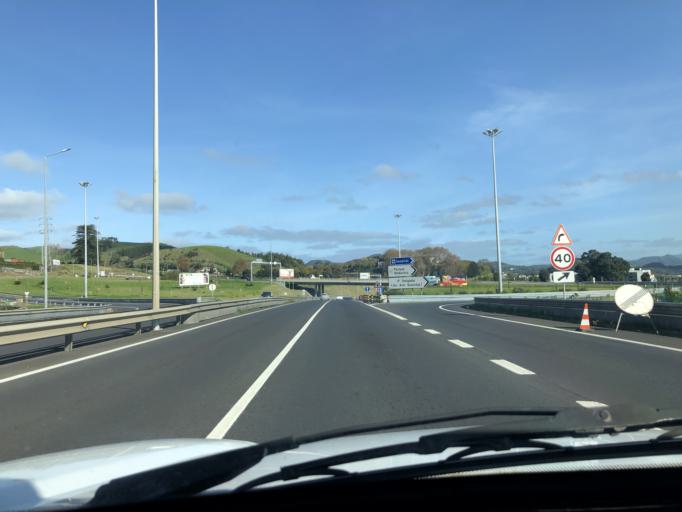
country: PT
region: Azores
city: Ponta Delgada
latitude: 37.7543
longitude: -25.6770
